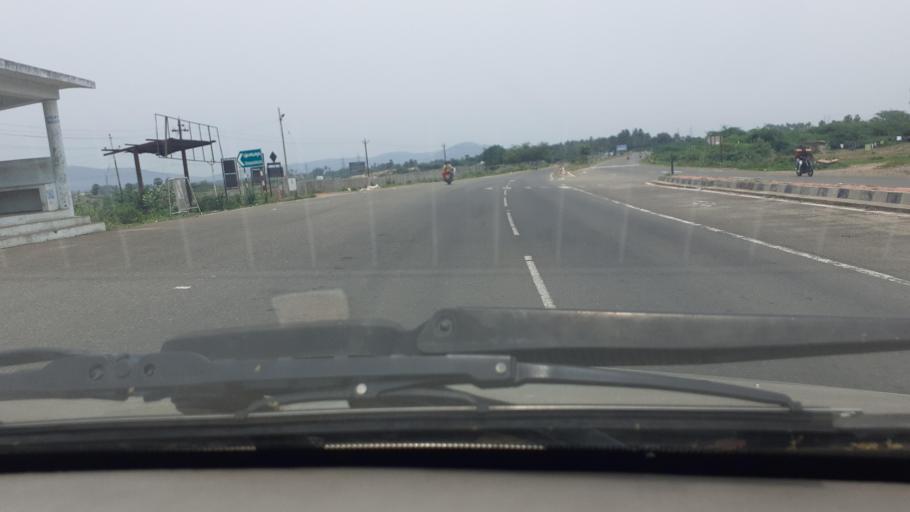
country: IN
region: Tamil Nadu
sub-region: Tirunelveli Kattabo
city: Tirunelveli
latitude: 8.7106
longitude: 77.8077
